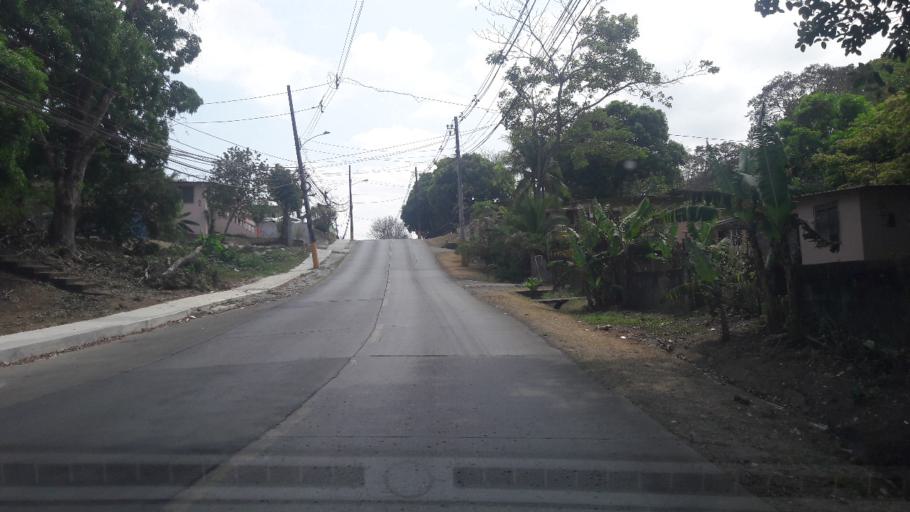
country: PA
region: Panama
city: La Cabima
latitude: 9.1267
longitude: -79.5455
